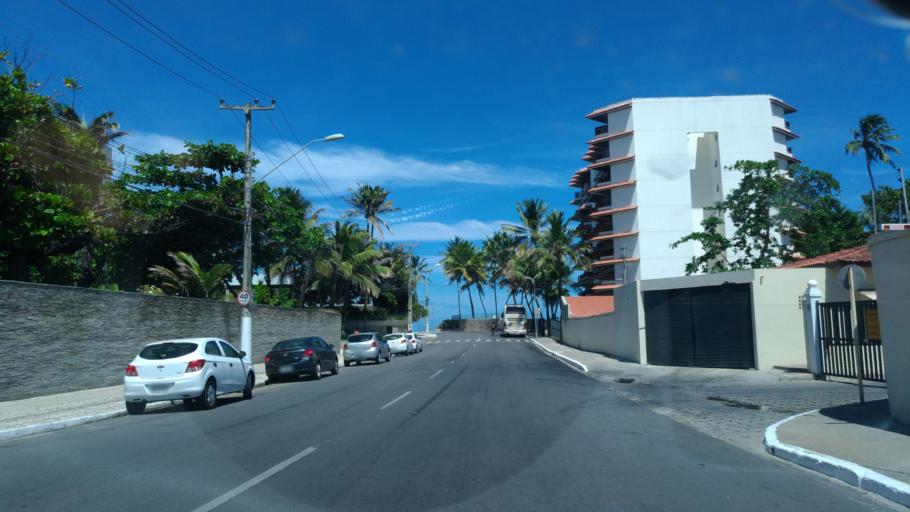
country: BR
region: Alagoas
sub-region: Maceio
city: Maceio
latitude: -9.6395
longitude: -35.6996
